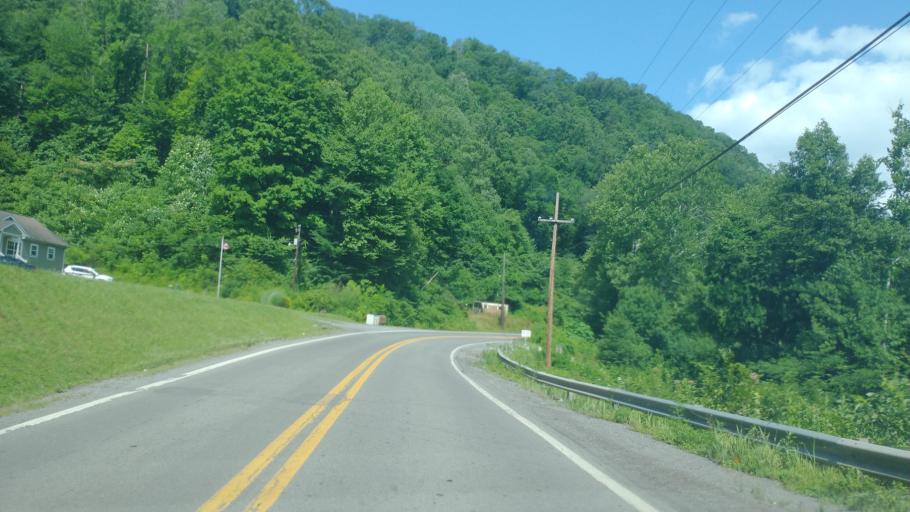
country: US
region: West Virginia
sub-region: McDowell County
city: Welch
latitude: 37.4188
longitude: -81.5426
